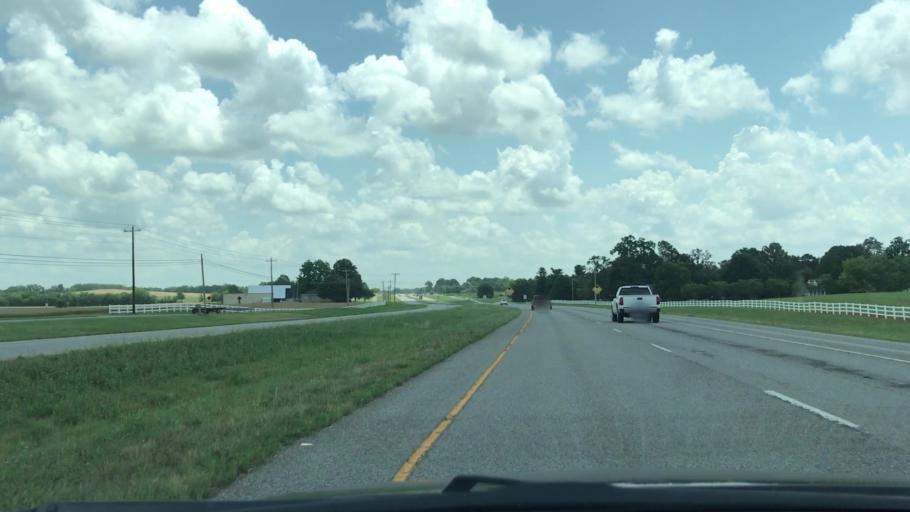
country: US
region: Kentucky
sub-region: Christian County
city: Hopkinsville
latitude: 36.8767
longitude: -87.5593
